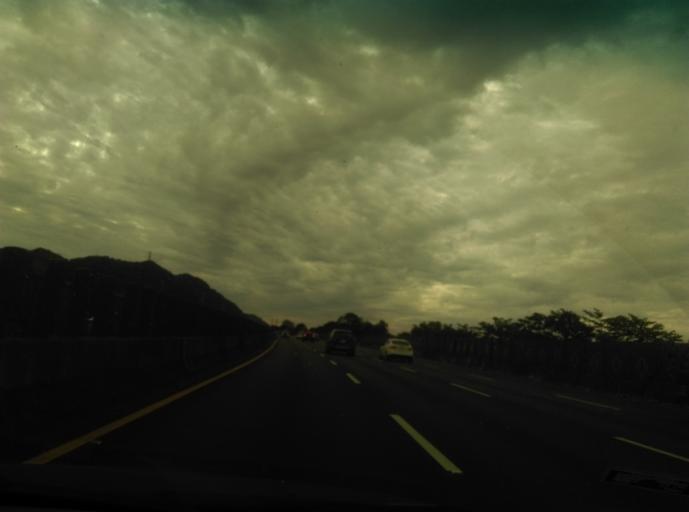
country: TW
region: Taiwan
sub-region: Taoyuan
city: Taoyuan
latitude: 24.9482
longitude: 121.3714
